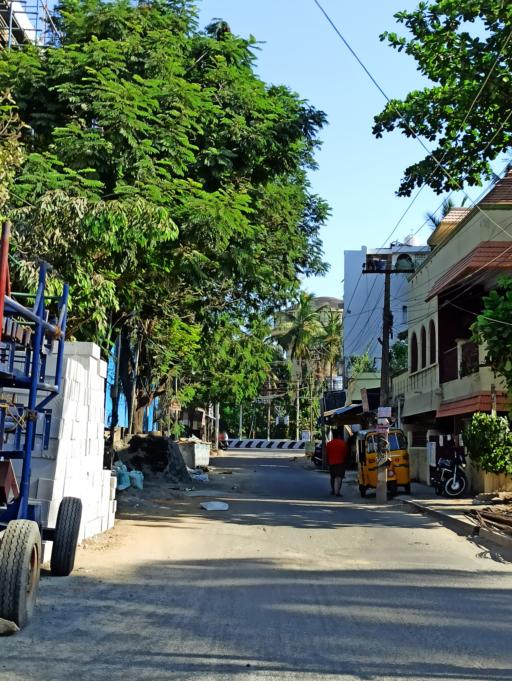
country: IN
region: Tamil Nadu
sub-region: Thiruvallur
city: Porur
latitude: 13.0339
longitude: 80.1623
